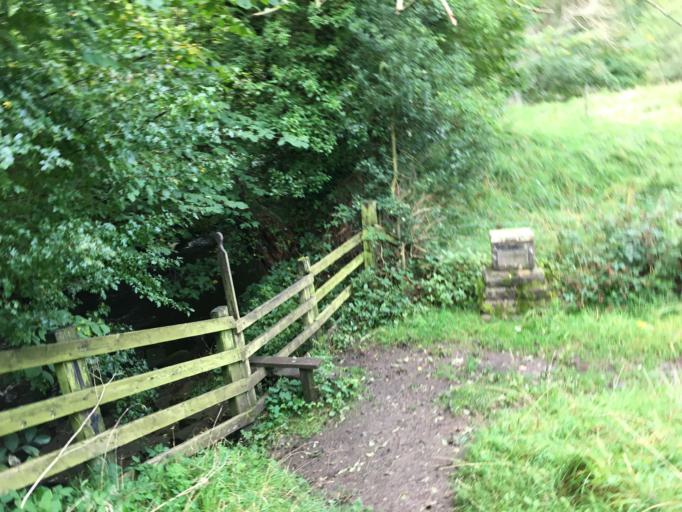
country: GB
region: England
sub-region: North Yorkshire
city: Sleights
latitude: 54.4085
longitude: -0.7378
